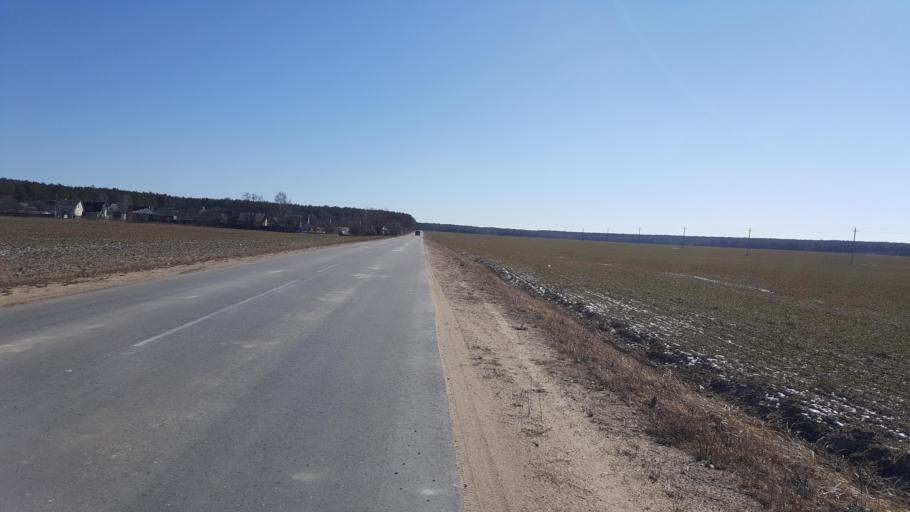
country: BY
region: Brest
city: Kamyanyets
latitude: 52.3700
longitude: 23.7982
